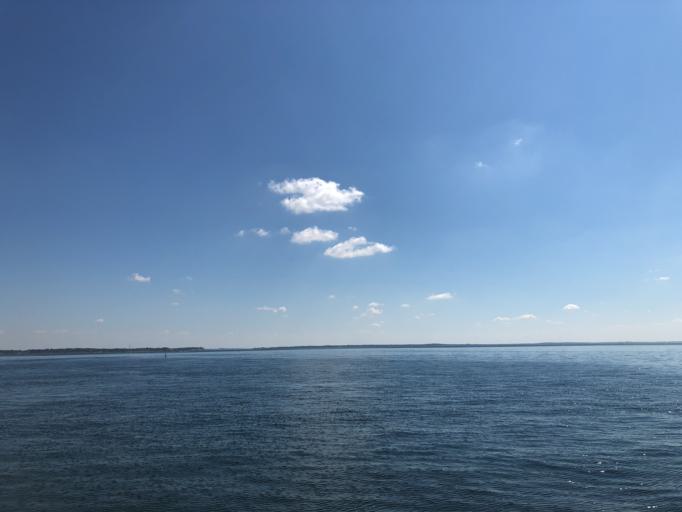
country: DK
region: Capital Region
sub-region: Halsnaes Kommune
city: Hundested
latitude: 55.9428
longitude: 11.7751
